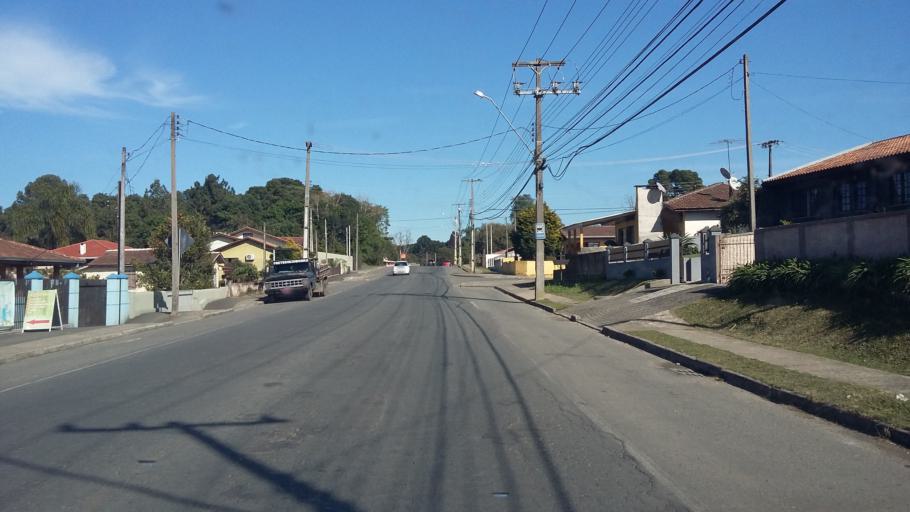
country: BR
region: Parana
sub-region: Campo Largo
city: Campo Largo
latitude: -25.4579
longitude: -49.5453
